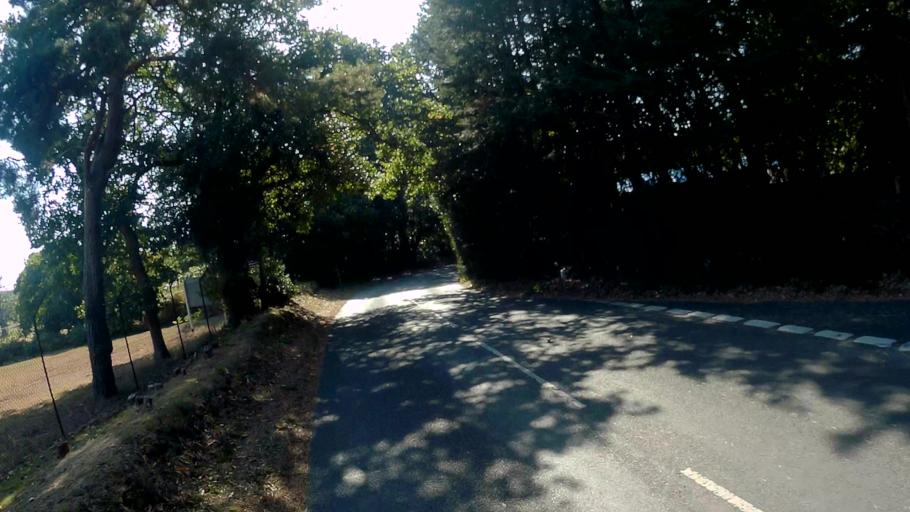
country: GB
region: England
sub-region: Surrey
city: Farnham
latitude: 51.1778
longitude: -0.7811
